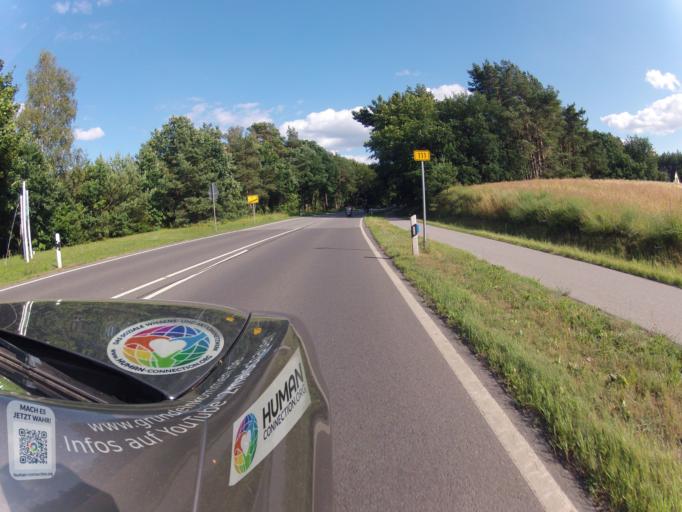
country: DE
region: Mecklenburg-Vorpommern
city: Loddin
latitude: 54.0098
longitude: 14.0556
